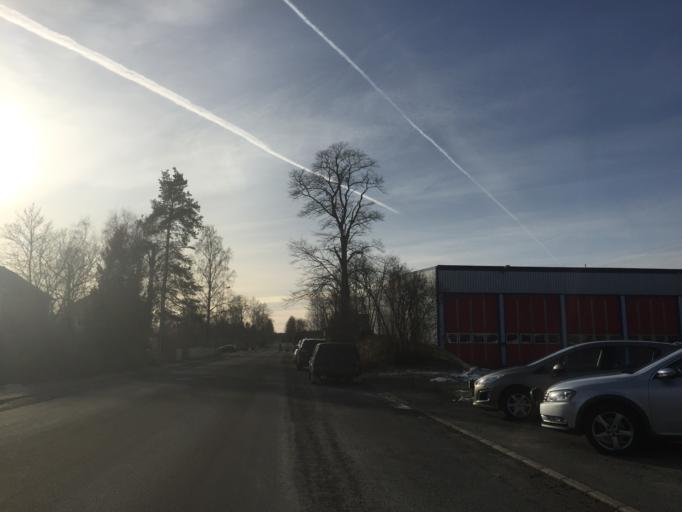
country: SE
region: Joenkoeping
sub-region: Aneby Kommun
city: Aneby
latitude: 57.8350
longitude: 14.8108
